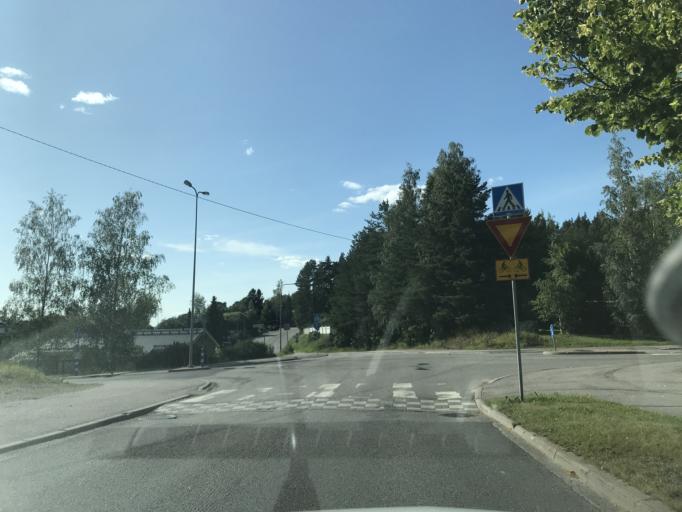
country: FI
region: Uusimaa
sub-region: Helsinki
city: Nurmijaervi
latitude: 60.3774
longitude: 24.7519
